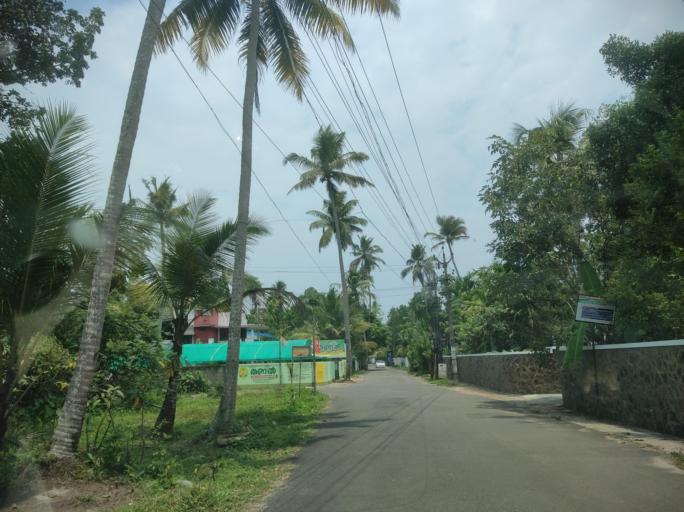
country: IN
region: Kerala
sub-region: Alappuzha
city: Vayalar
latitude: 9.7316
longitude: 76.3279
